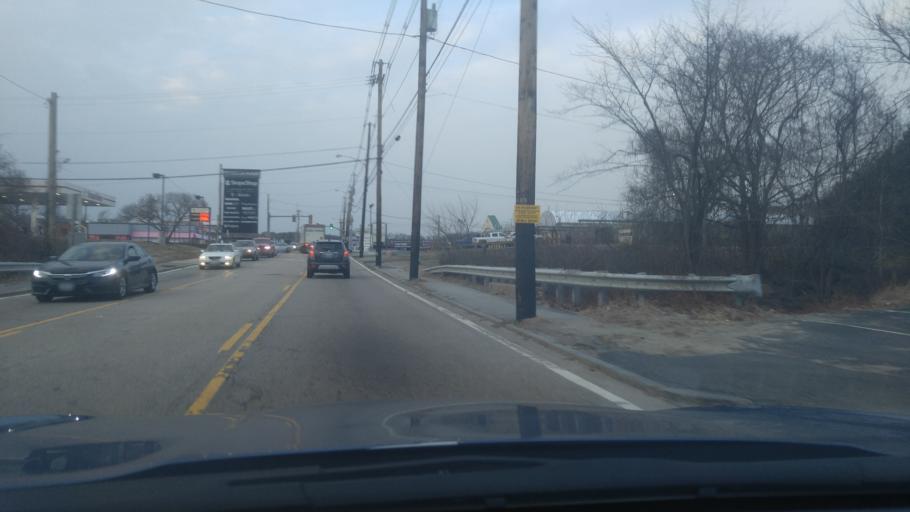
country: US
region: Rhode Island
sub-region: Providence County
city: Johnston
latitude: 41.8191
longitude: -71.4974
